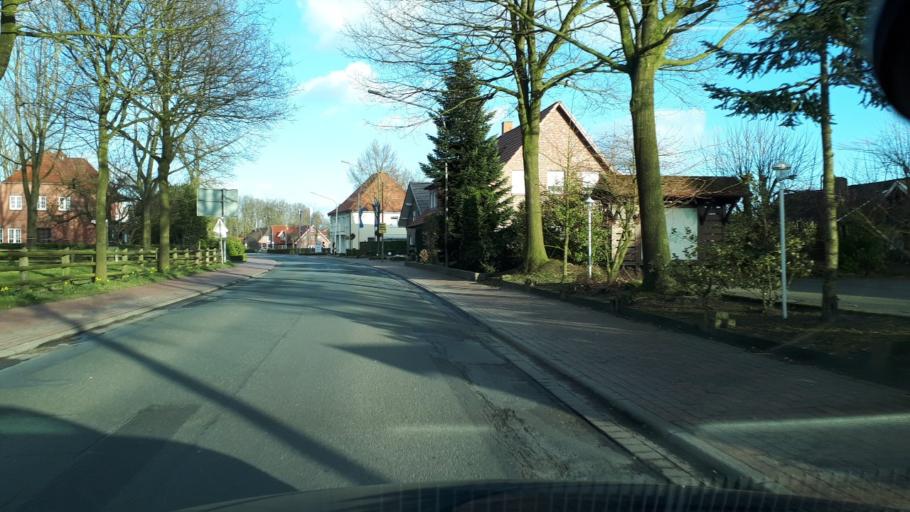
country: DE
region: Lower Saxony
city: Vrees
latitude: 52.8831
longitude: 7.8370
